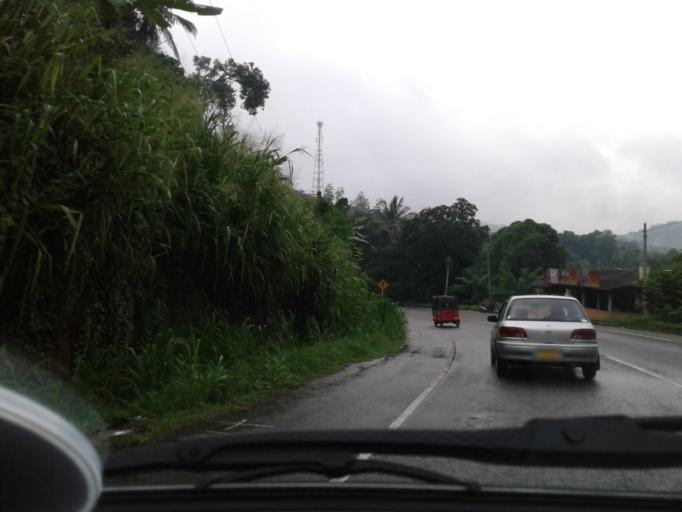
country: LK
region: Central
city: Kadugannawa
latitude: 7.2363
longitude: 80.2684
